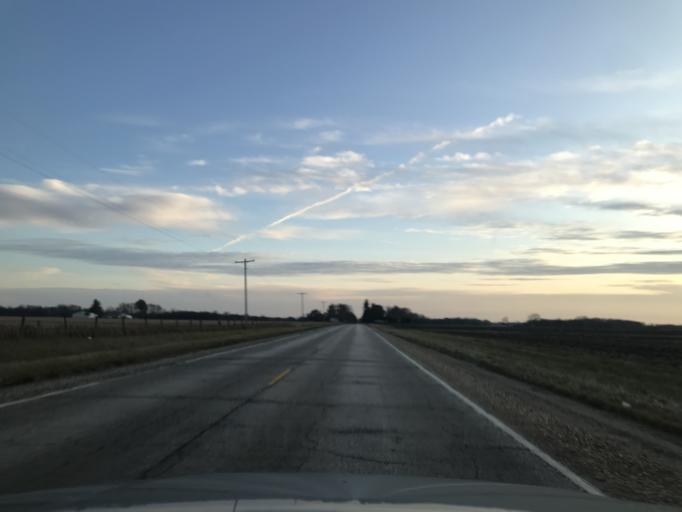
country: US
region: Illinois
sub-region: Henderson County
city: Oquawka
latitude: 40.9470
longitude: -90.8640
